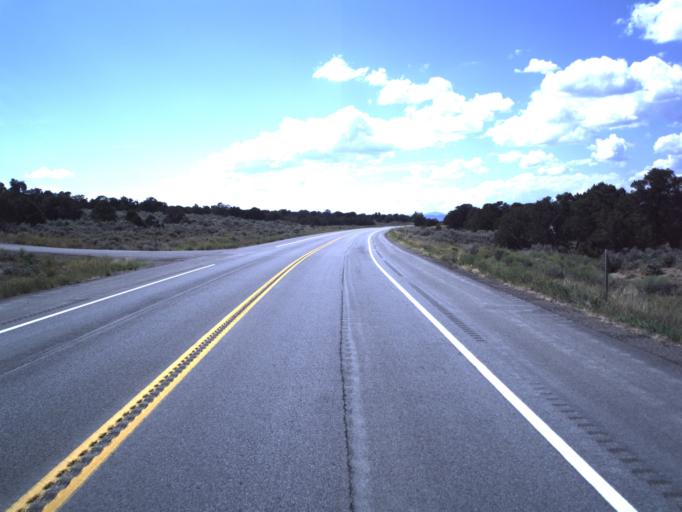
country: US
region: Utah
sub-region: Duchesne County
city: Duchesne
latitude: 40.1837
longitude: -110.6630
